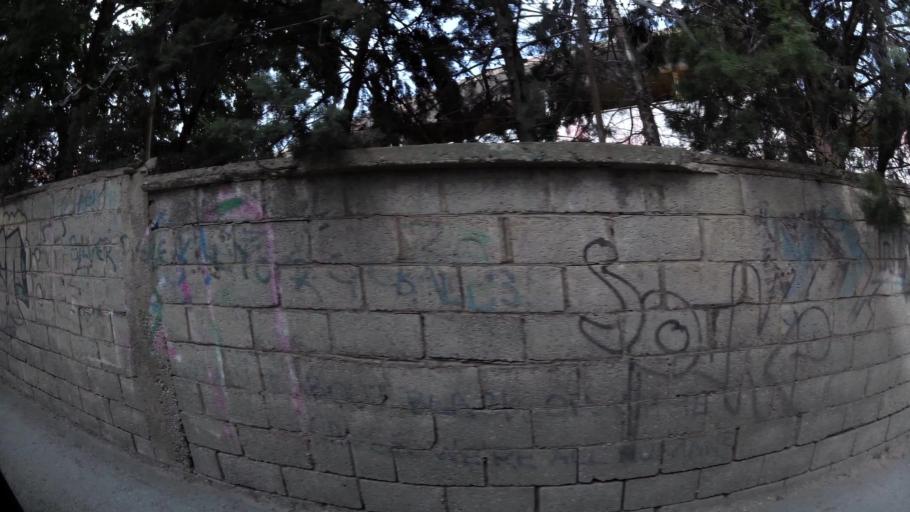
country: GR
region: Central Macedonia
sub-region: Nomos Thessalonikis
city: Stavroupoli
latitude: 40.6857
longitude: 22.9306
